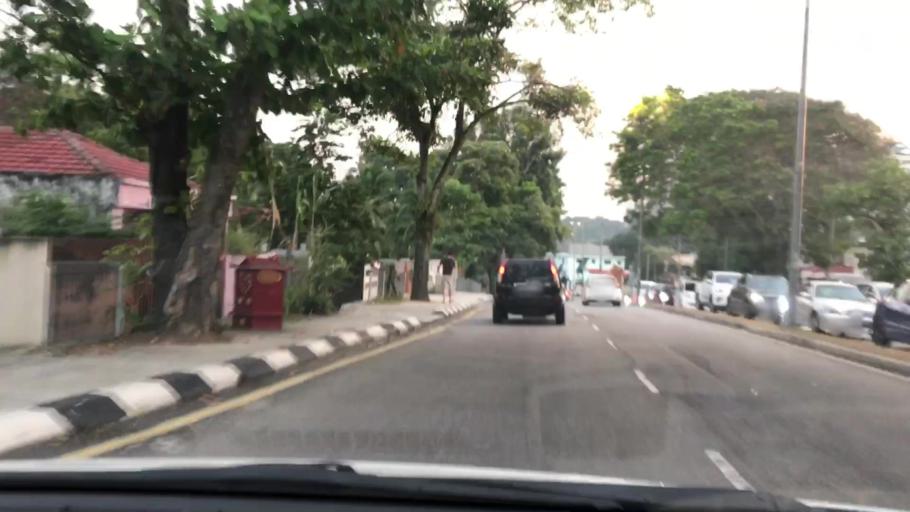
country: MY
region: Selangor
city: Kampong Baharu Balakong
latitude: 3.0664
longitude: 101.6947
